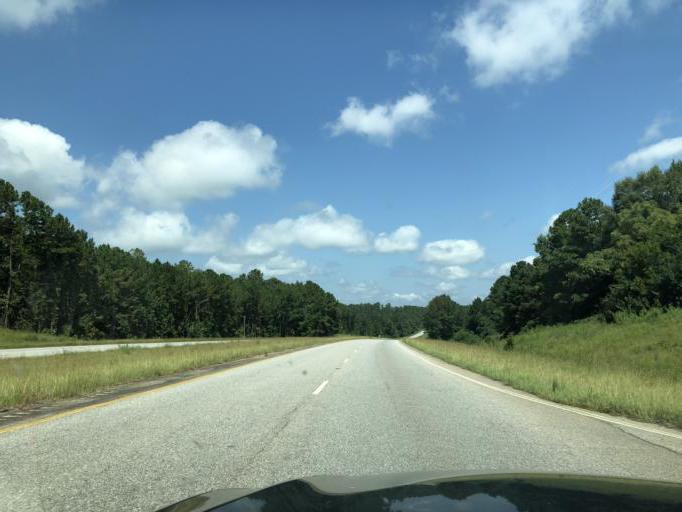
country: US
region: Alabama
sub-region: Henry County
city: Abbeville
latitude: 31.6381
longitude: -85.2805
